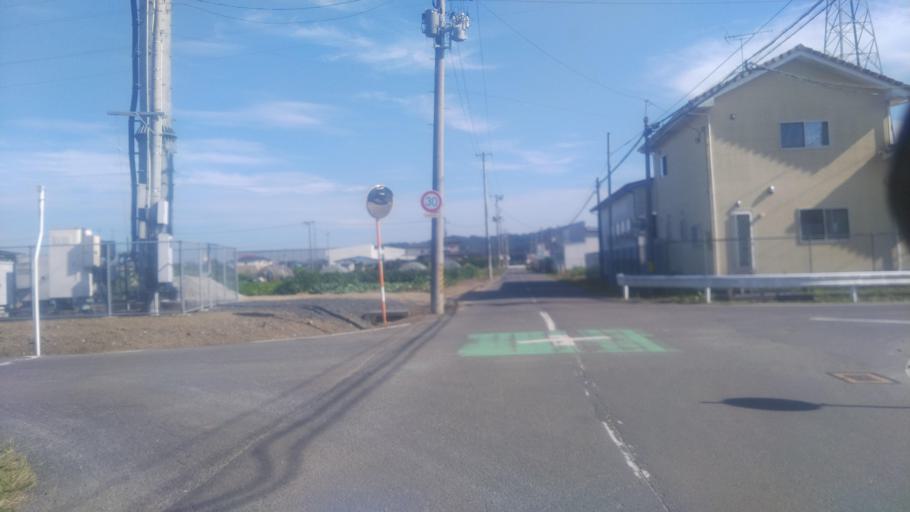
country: JP
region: Miyagi
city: Okawara
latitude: 38.0464
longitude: 140.7036
